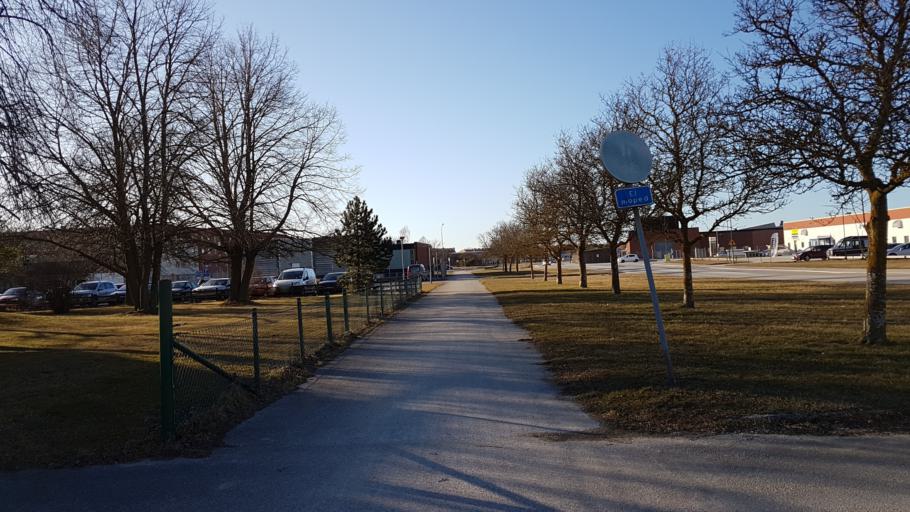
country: SE
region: Gotland
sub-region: Gotland
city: Visby
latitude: 57.6417
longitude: 18.3182
